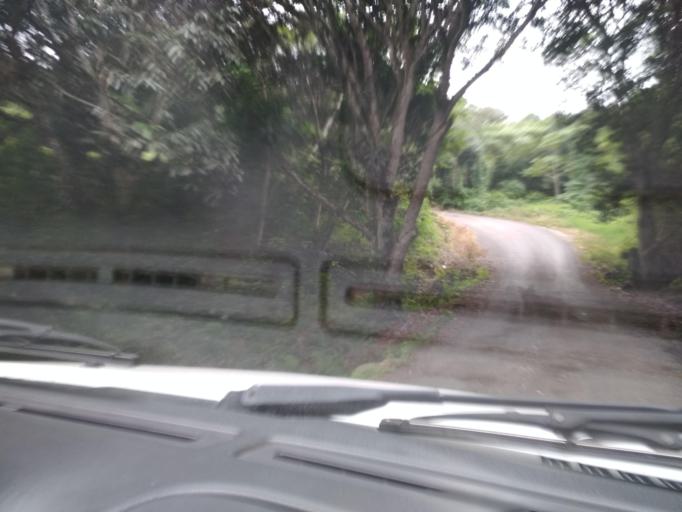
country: MX
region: Veracruz
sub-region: Actopan
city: Trapiche del Rosario
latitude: 19.5628
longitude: -96.7928
